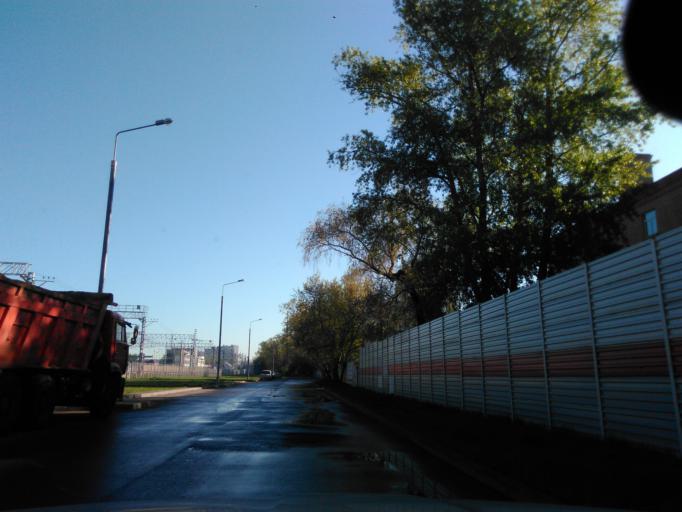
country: RU
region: Moskovskaya
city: Koptevo
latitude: 55.8344
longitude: 37.5133
